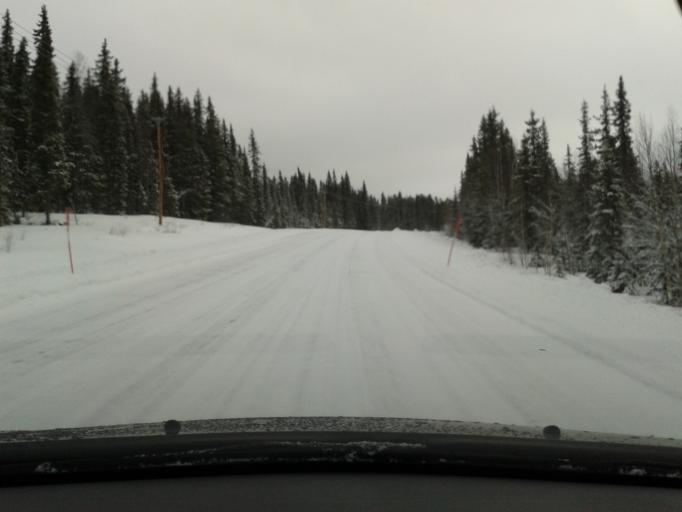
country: SE
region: Vaesterbotten
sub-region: Vilhelmina Kommun
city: Sjoberg
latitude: 65.2367
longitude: 15.8307
